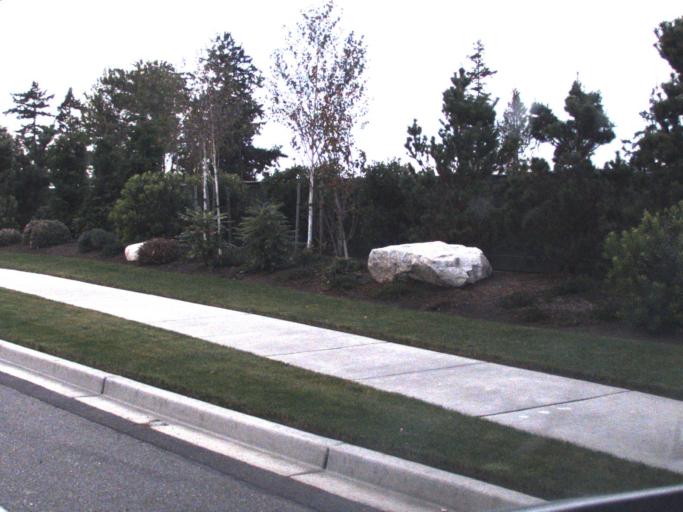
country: US
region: Washington
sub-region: Jefferson County
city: Port Hadlock-Irondale
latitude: 48.0464
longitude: -122.8198
